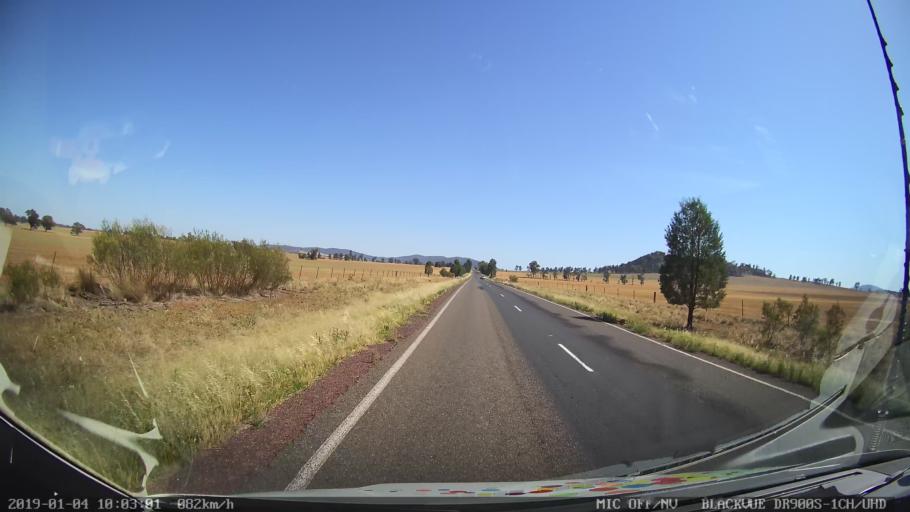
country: AU
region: New South Wales
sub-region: Cabonne
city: Canowindra
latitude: -33.4692
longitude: 148.3648
